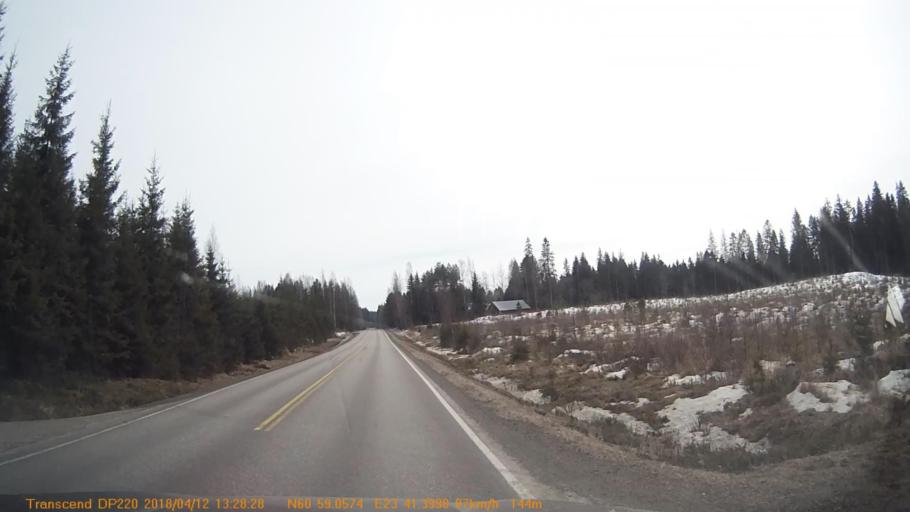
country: FI
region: Pirkanmaa
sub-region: Etelae-Pirkanmaa
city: Kylmaekoski
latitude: 60.9841
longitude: 23.6901
